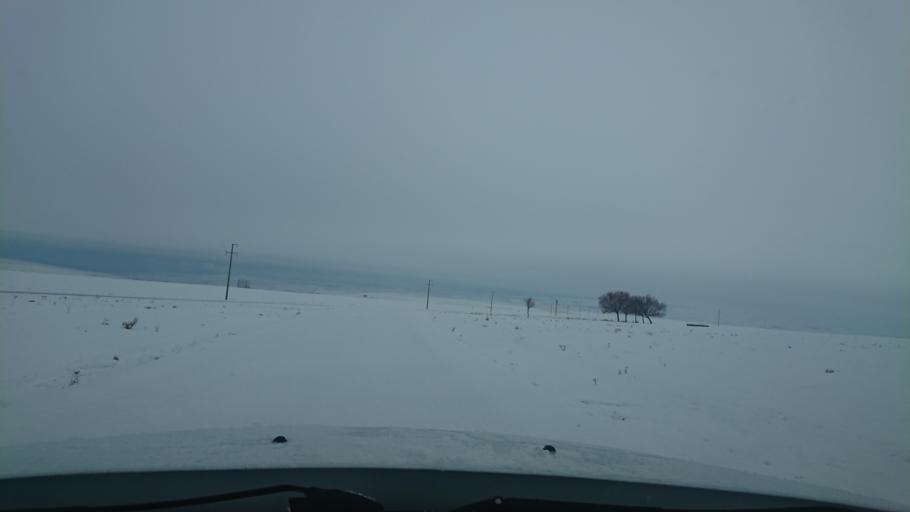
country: TR
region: Aksaray
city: Agacoren
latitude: 38.7208
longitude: 33.8667
